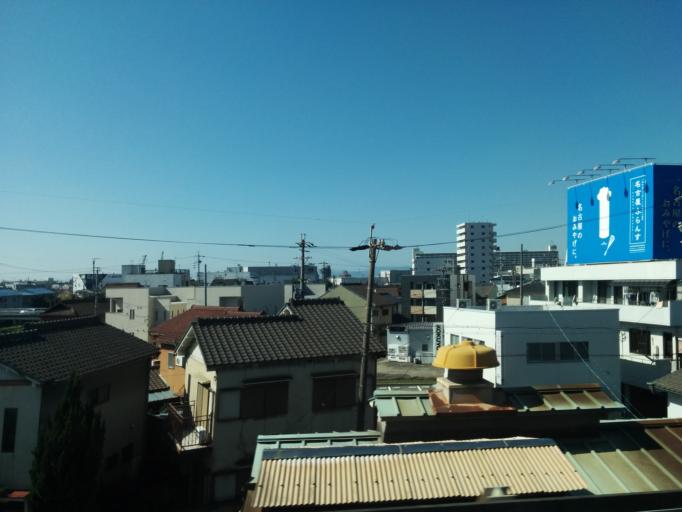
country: JP
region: Aichi
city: Nagoya-shi
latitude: 35.1547
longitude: 136.8874
